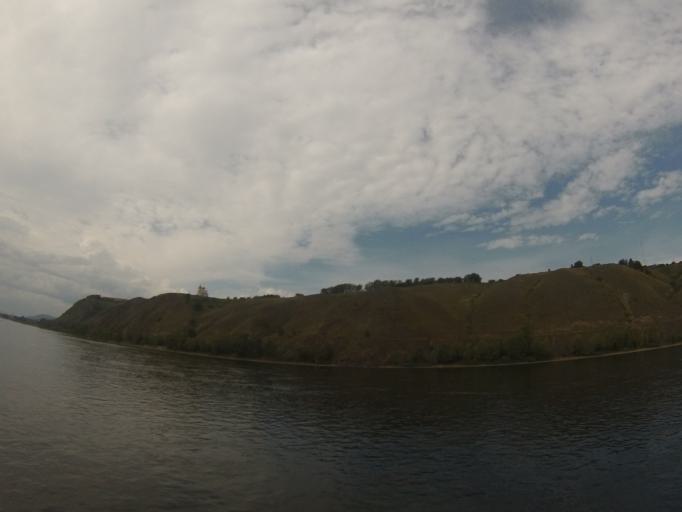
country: RU
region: Krasnoyarskiy
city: Krasnoyarsk
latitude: 55.9821
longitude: 92.7781
